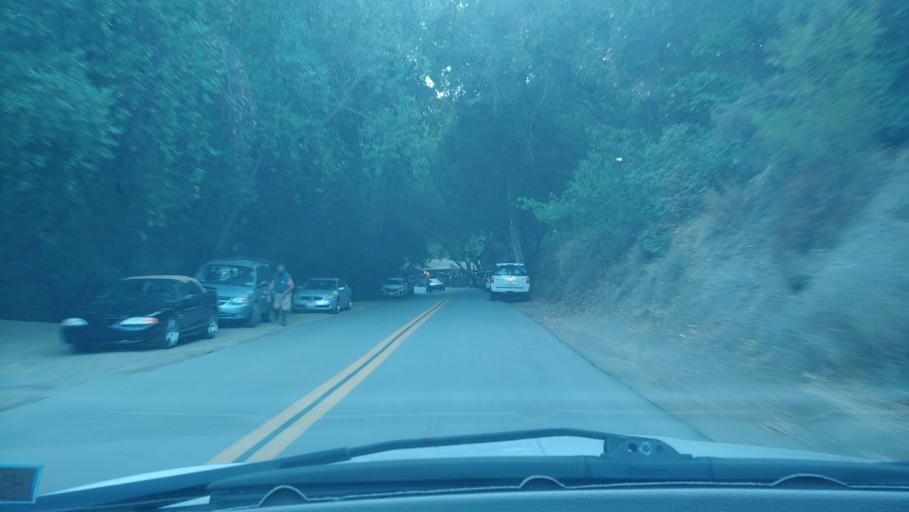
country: US
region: California
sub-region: Santa Barbara County
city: Goleta
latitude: 34.5225
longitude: -119.8395
